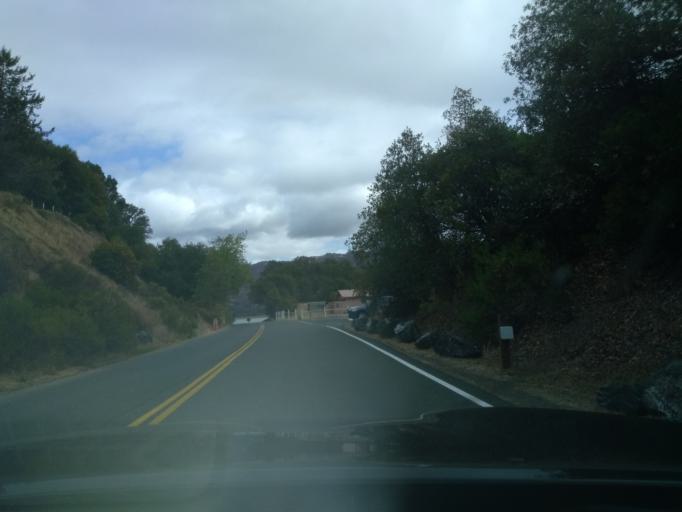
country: US
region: California
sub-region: Mendocino County
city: Ukiah
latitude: 39.2034
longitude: -123.1860
